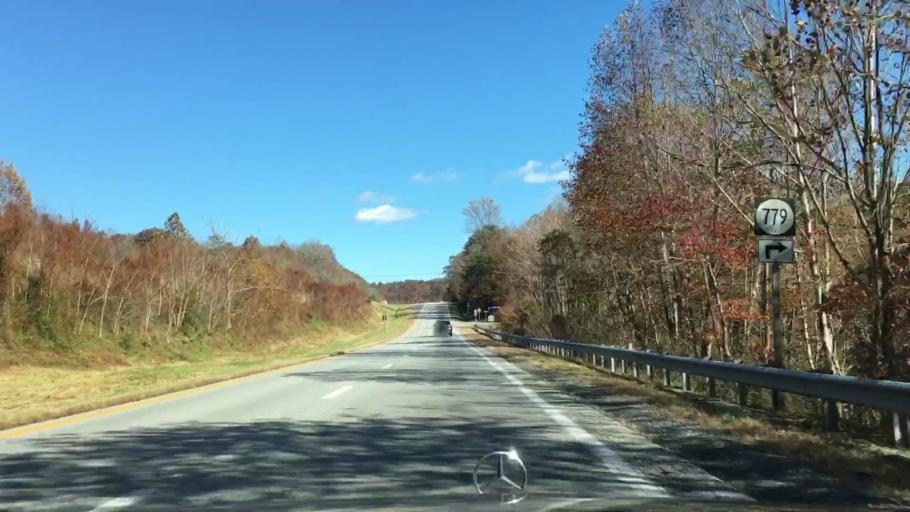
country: US
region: Virginia
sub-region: Nelson County
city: Nellysford
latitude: 37.8447
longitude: -78.7698
